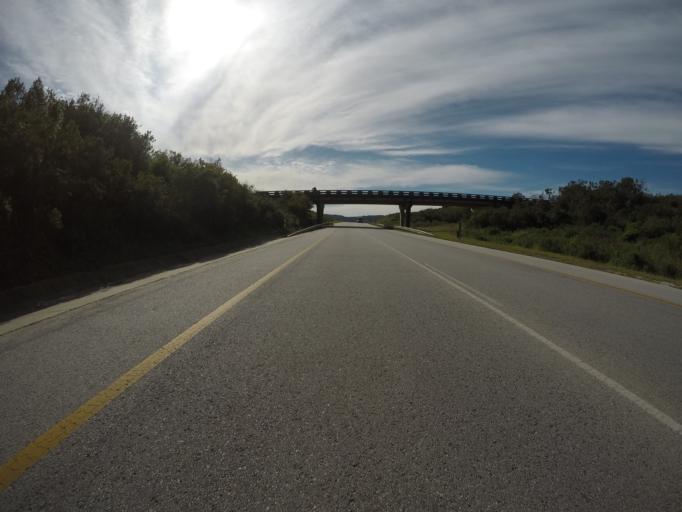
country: ZA
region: Eastern Cape
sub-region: Cacadu District Municipality
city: Jeffrey's Bay
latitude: -33.8974
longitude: 25.1207
